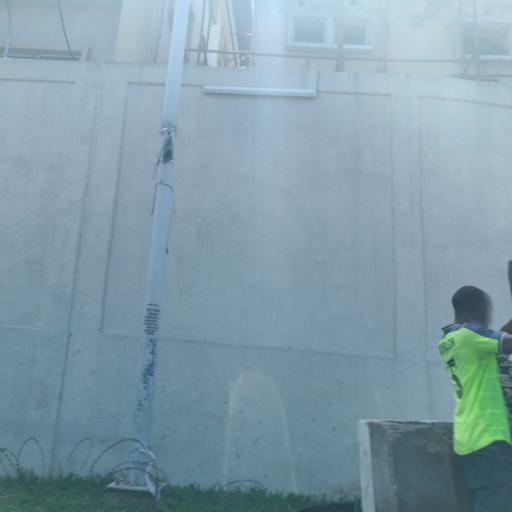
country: NG
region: Lagos
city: Lagos
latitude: 6.4649
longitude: 3.3898
